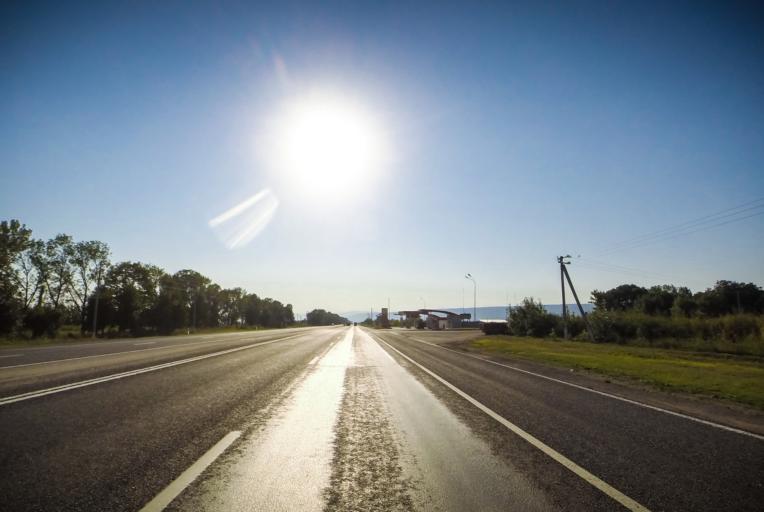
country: RU
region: Kabardino-Balkariya
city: Urukh
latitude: 43.3218
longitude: 44.0756
